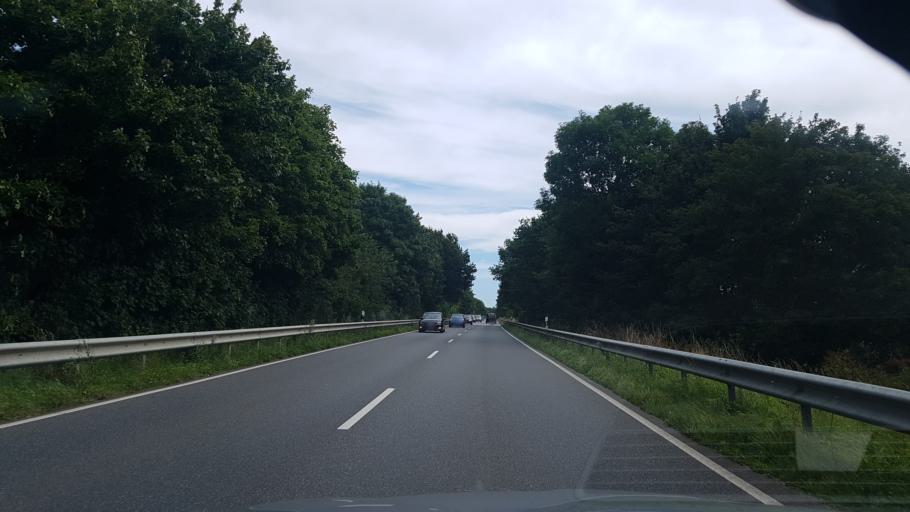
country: DE
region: Schleswig-Holstein
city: Bordesholm
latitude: 54.1868
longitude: 10.0099
